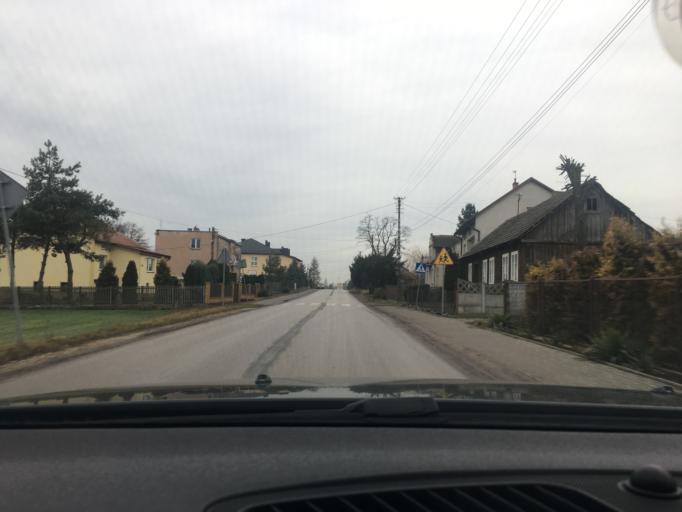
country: PL
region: Swietokrzyskie
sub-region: Powiat jedrzejowski
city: Jedrzejow
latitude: 50.6408
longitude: 20.3767
